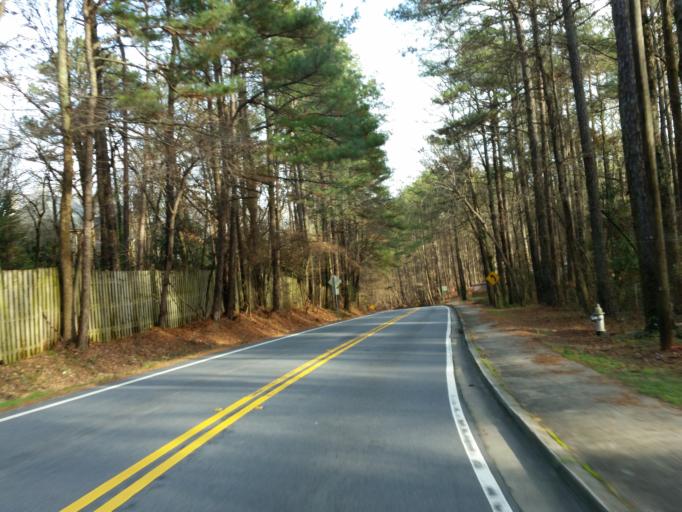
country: US
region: Georgia
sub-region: Fulton County
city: Sandy Springs
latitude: 33.9386
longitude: -84.4452
